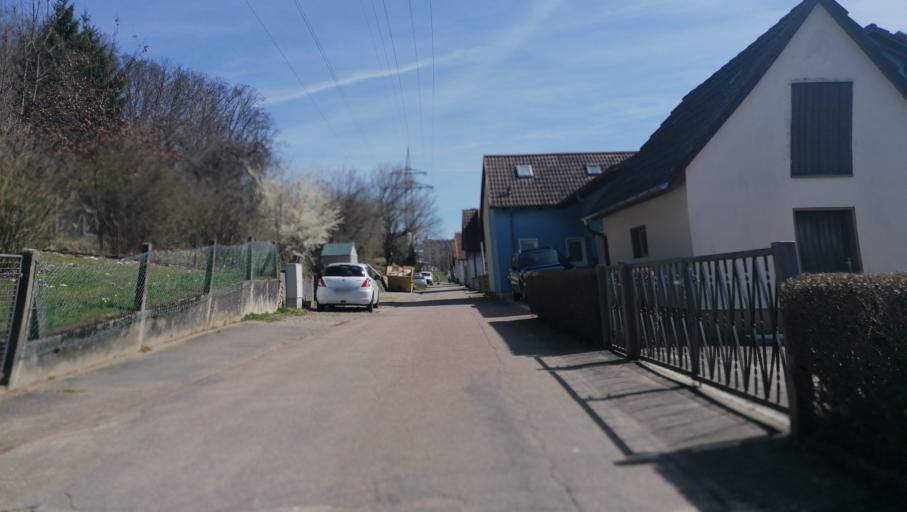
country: DE
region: Baden-Wuerttemberg
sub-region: Freiburg Region
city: Bad Sackingen
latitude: 47.5617
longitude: 7.9340
